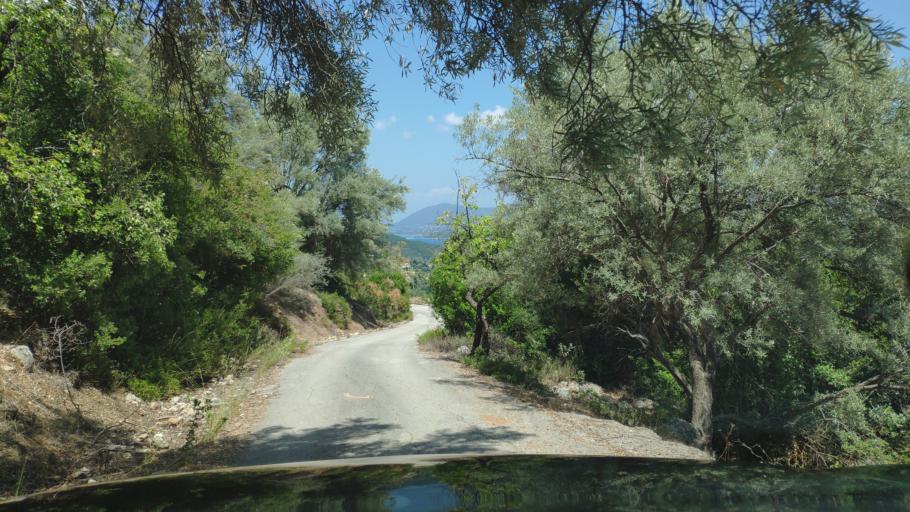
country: GR
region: Ionian Islands
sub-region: Lefkada
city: Nidri
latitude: 38.7529
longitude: 20.7129
